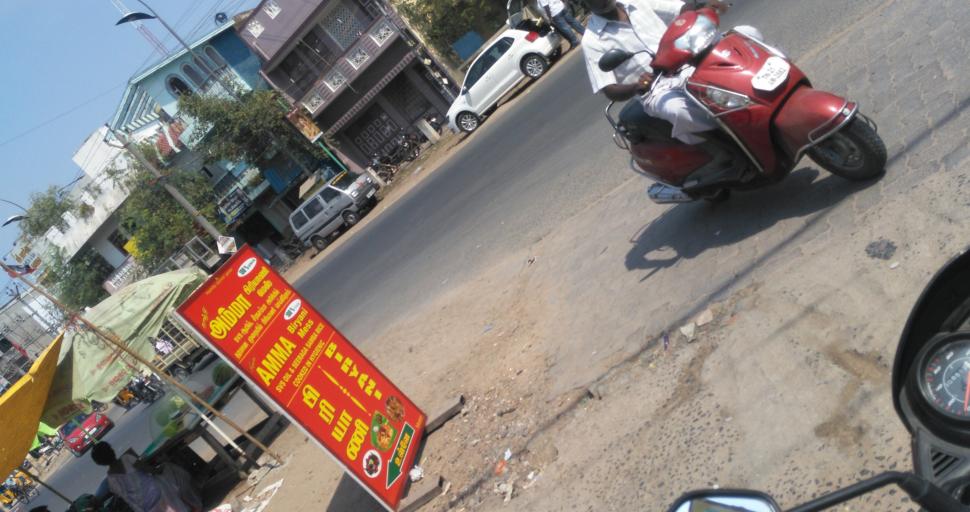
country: IN
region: Tamil Nadu
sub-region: Kancheepuram
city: Kanchipuram
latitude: 12.8410
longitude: 79.7057
